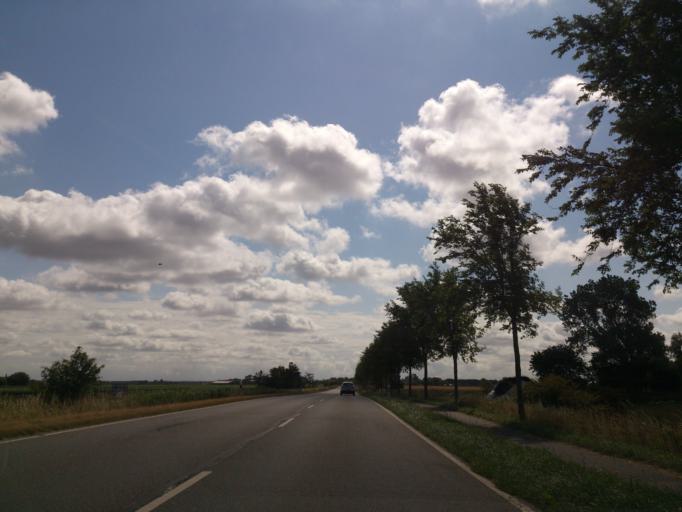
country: DE
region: Schleswig-Holstein
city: Grothusenkoog
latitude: 54.3035
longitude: 8.7637
